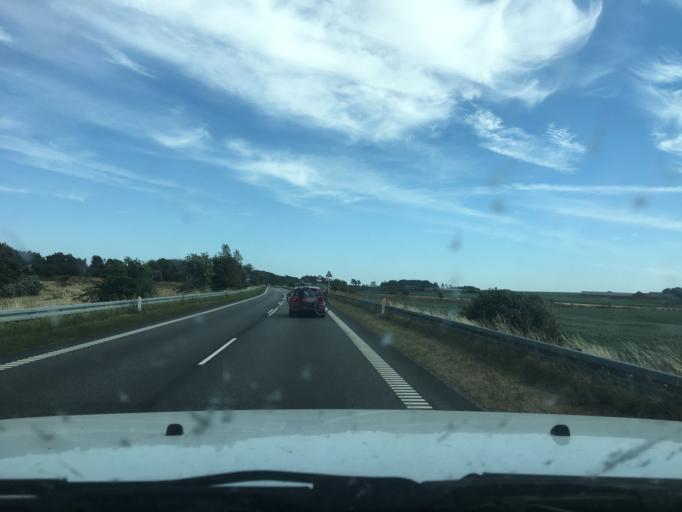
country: DK
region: Central Jutland
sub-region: Viborg Kommune
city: Viborg
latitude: 56.5521
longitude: 9.3914
